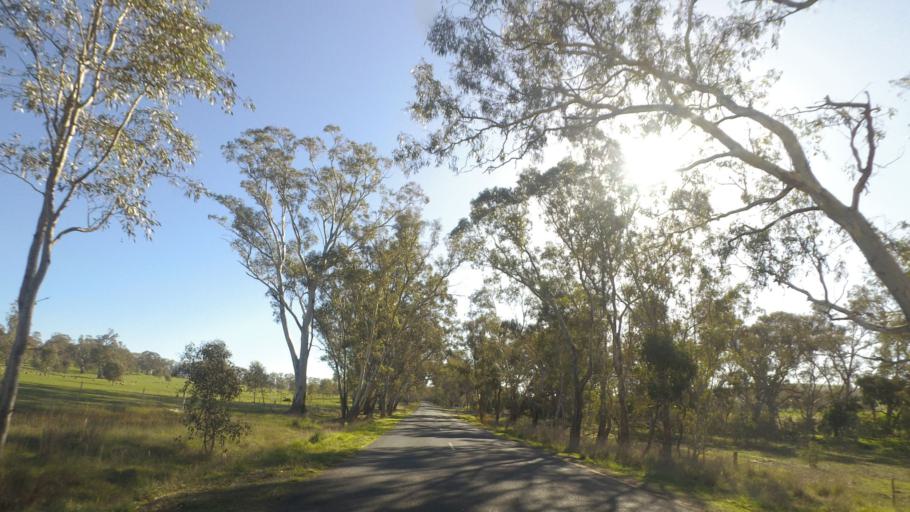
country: AU
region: Victoria
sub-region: Mount Alexander
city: Castlemaine
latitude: -36.9588
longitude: 144.3492
